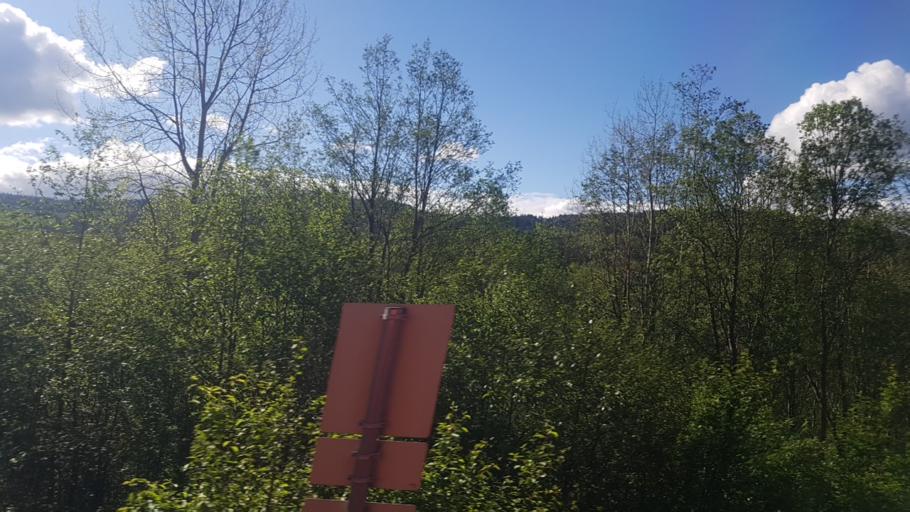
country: NO
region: Sor-Trondelag
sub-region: Midtre Gauldal
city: Storen
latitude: 62.9699
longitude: 10.2041
